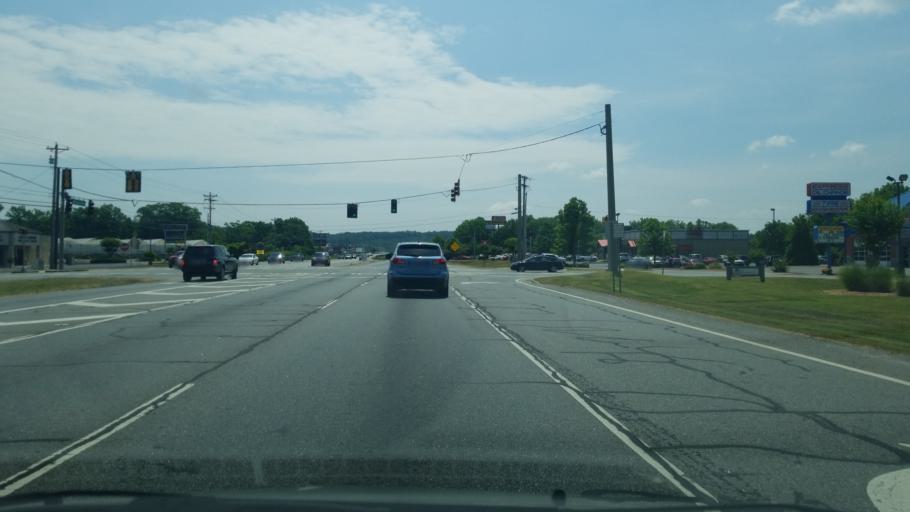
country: US
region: Georgia
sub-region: Catoosa County
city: Fort Oglethorpe
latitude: 34.9428
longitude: -85.2232
